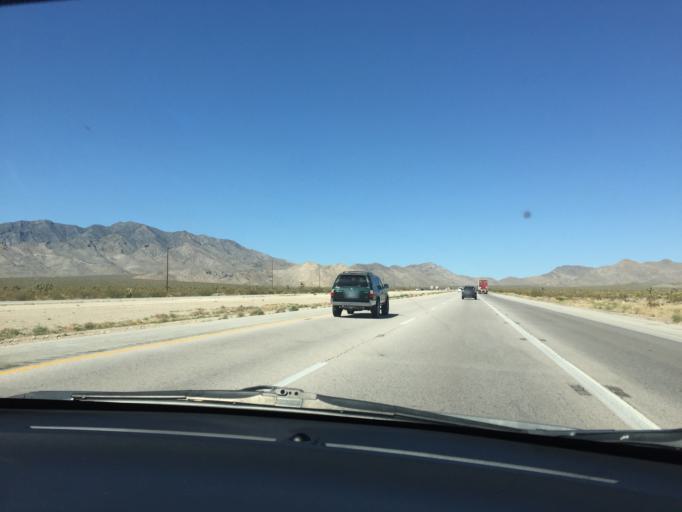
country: US
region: Nevada
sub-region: Clark County
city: Sandy Valley
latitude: 35.4535
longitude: -115.6468
